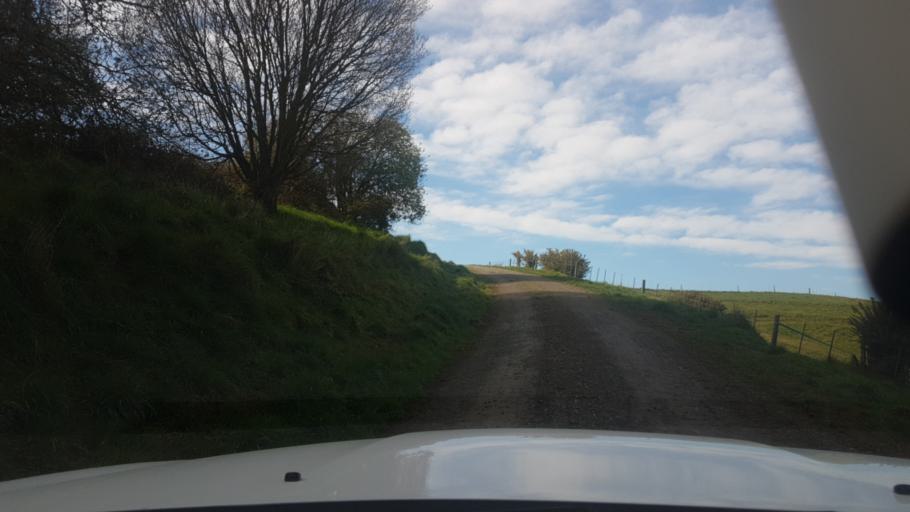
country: NZ
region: Canterbury
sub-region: Timaru District
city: Pleasant Point
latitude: -44.1958
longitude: 171.1882
